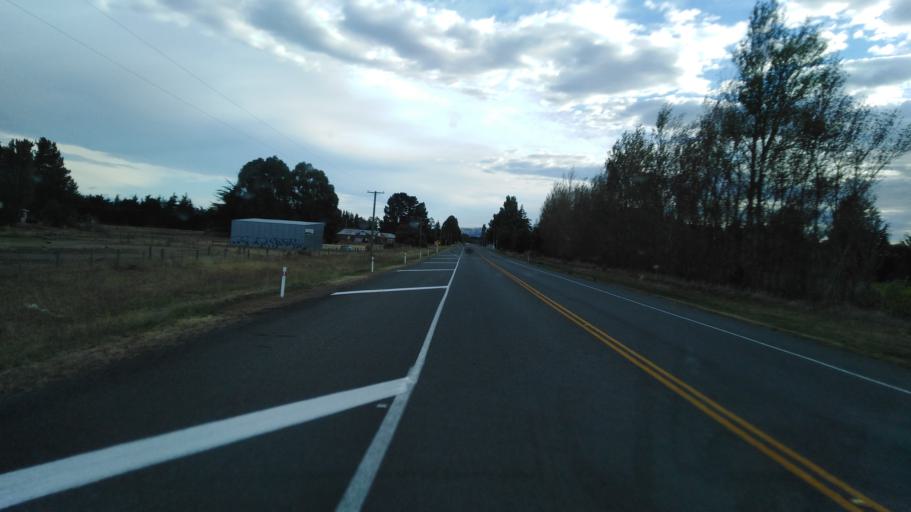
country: NZ
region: Canterbury
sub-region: Hurunui District
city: Amberley
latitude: -43.2297
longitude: 172.7257
